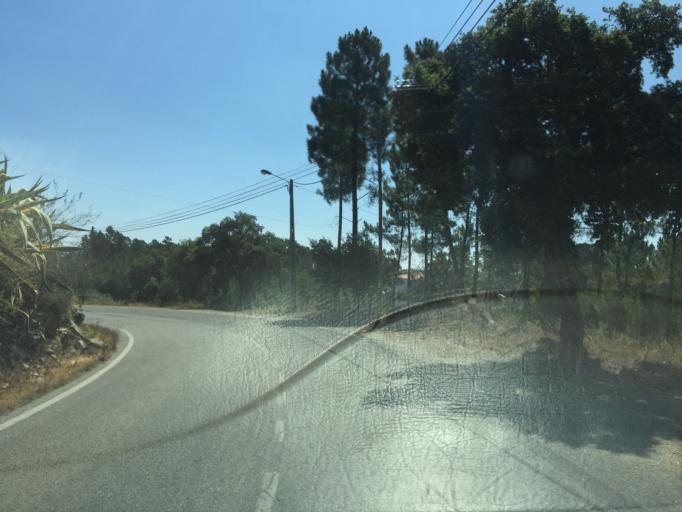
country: PT
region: Castelo Branco
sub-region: Proenca-A-Nova
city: Proenca-a-Nova
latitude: 39.7463
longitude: -7.9086
